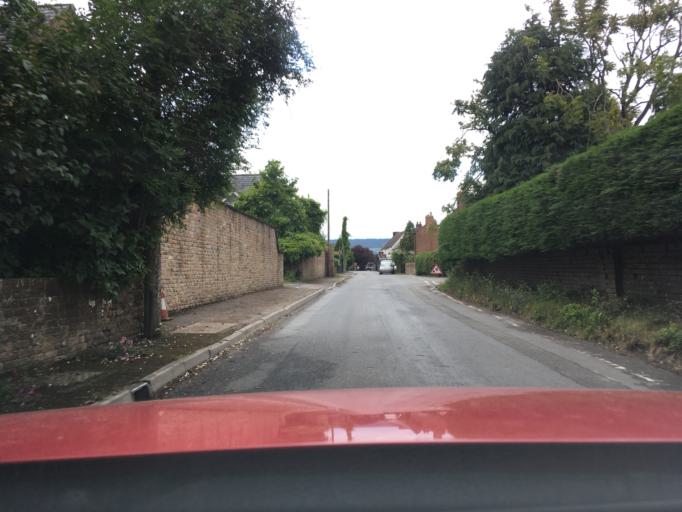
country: GB
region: England
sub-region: Gloucestershire
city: Cinderford
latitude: 51.7961
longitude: -2.4227
